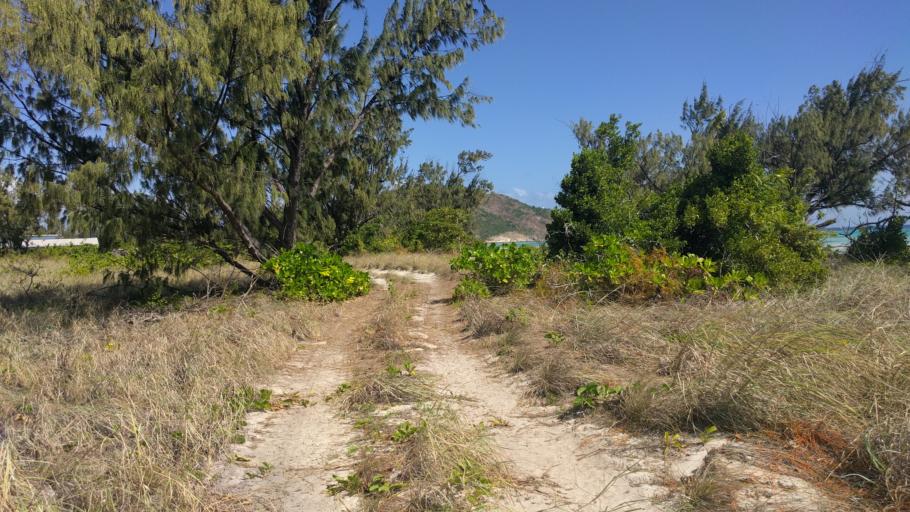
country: AU
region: Queensland
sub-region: Cook
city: Cooktown
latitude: -14.6777
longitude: 145.4475
